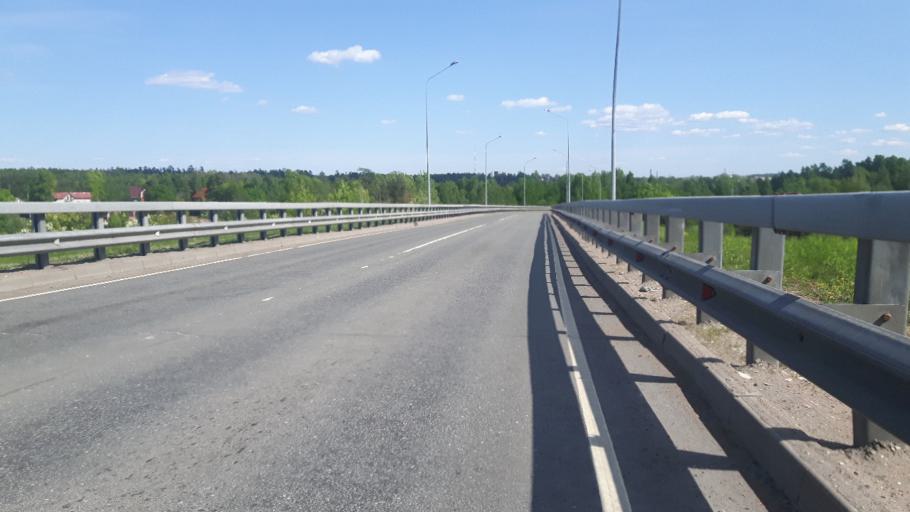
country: RU
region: Leningrad
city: Vyborg
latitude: 60.7363
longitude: 28.6936
